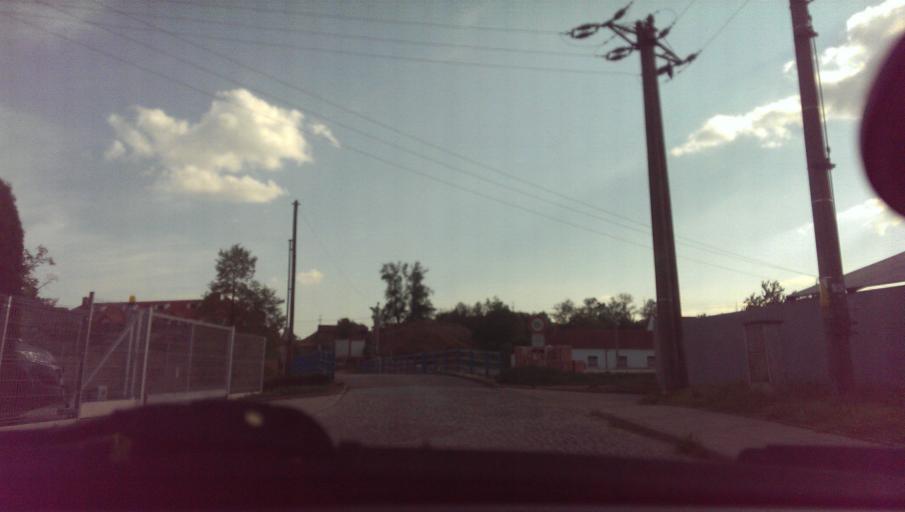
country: CZ
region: Zlin
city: Uhersky Brod
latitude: 49.0166
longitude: 17.6443
